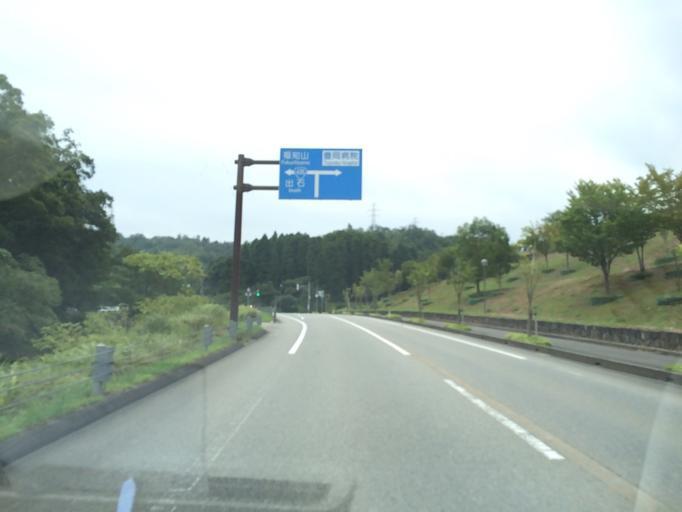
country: JP
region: Hyogo
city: Toyooka
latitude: 35.5275
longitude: 134.8087
